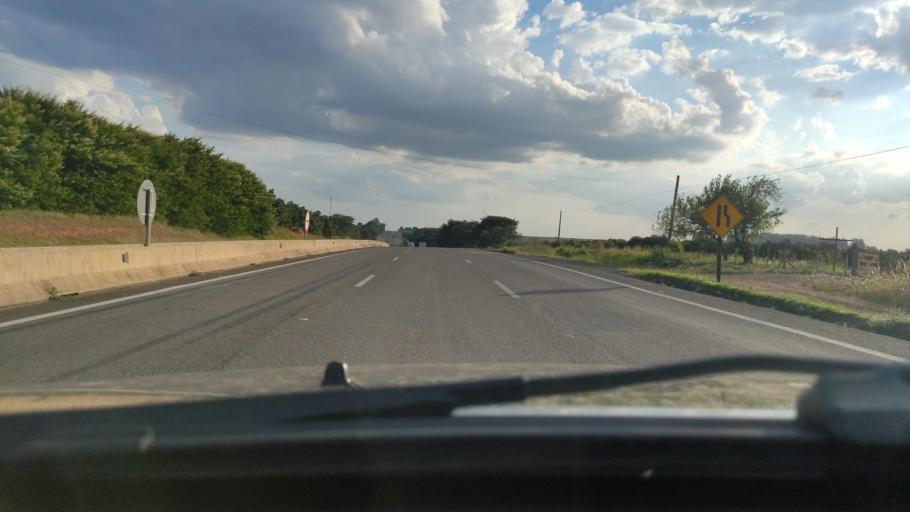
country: BR
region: Sao Paulo
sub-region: Mogi-Mirim
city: Mogi Mirim
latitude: -22.4569
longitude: -47.0950
